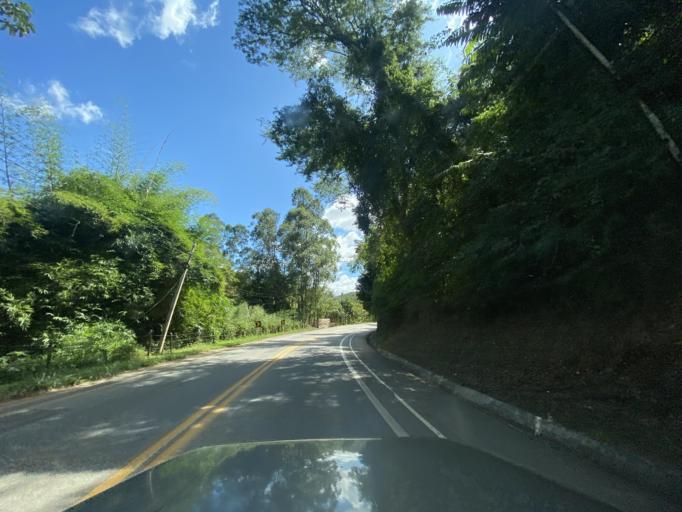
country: BR
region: Espirito Santo
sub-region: Alegre
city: Alegre
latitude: -20.7649
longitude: -41.5123
